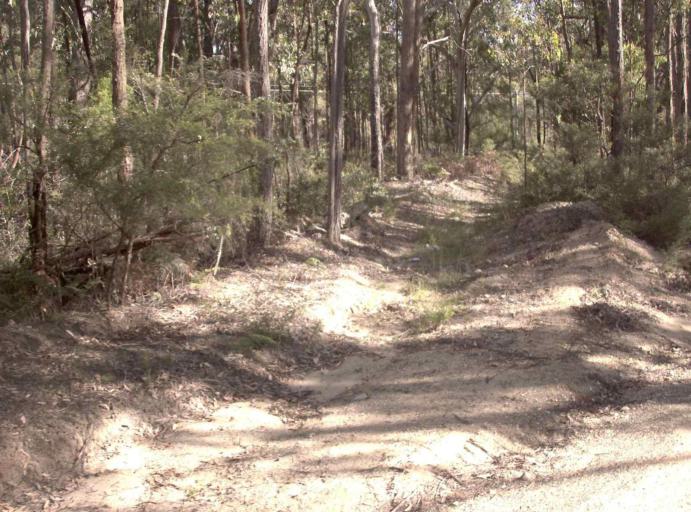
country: AU
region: Victoria
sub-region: East Gippsland
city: Lakes Entrance
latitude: -37.6863
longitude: 148.0493
